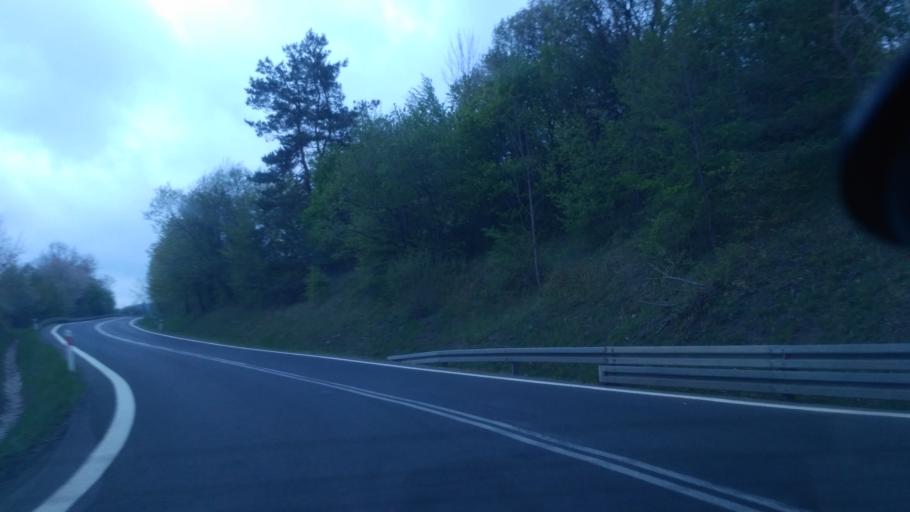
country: PL
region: Subcarpathian Voivodeship
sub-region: Powiat sanocki
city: Tyrawa Woloska
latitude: 49.5498
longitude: 22.3216
